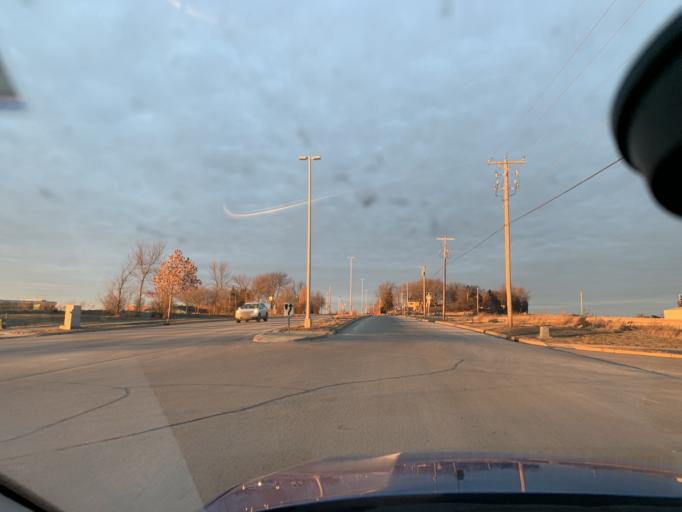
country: US
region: Wisconsin
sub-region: Dane County
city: Middleton
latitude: 43.0576
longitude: -89.5520
